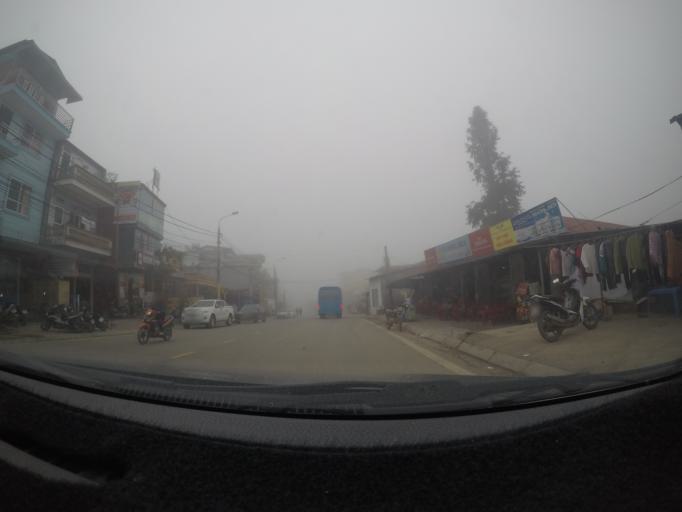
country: VN
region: Lao Cai
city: Sa Pa
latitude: 22.3404
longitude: 103.8460
